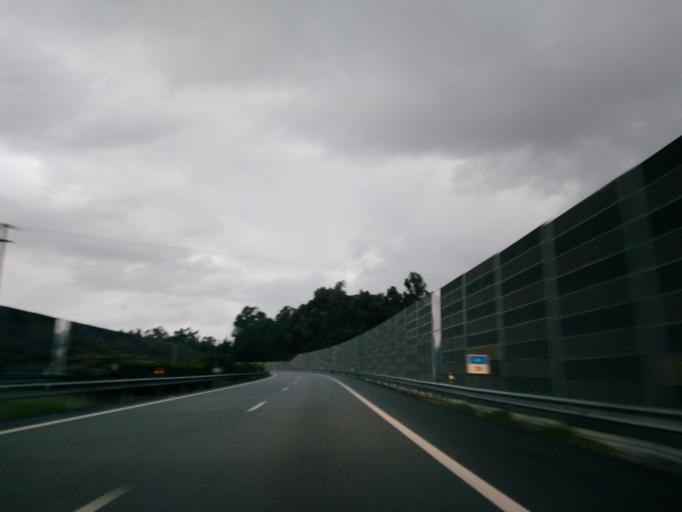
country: PT
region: Braga
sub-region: Vila Nova de Famalicao
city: Vila Nova de Famalicao
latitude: 41.4018
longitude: -8.4943
